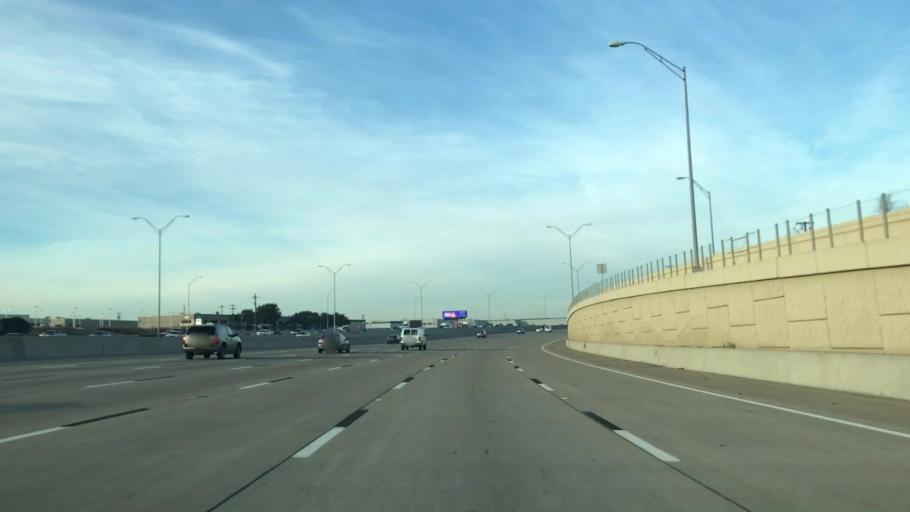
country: US
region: Texas
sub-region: Tarrant County
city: Grapevine
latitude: 32.9235
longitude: -97.0612
